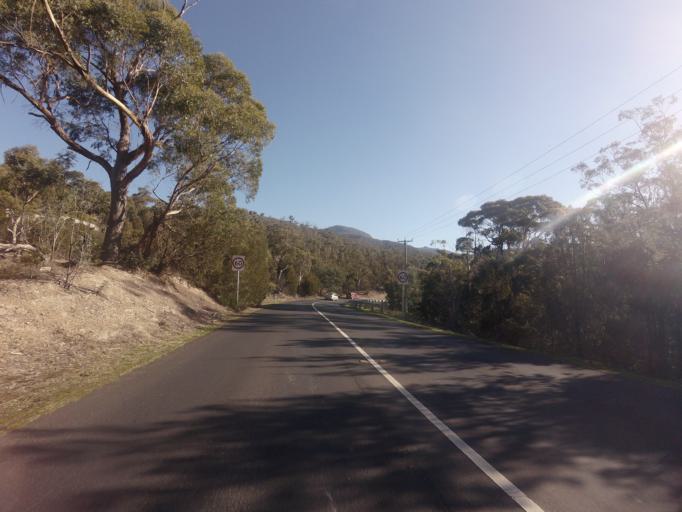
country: AU
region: Tasmania
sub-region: Glenorchy
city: West Moonah
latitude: -42.8627
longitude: 147.2743
